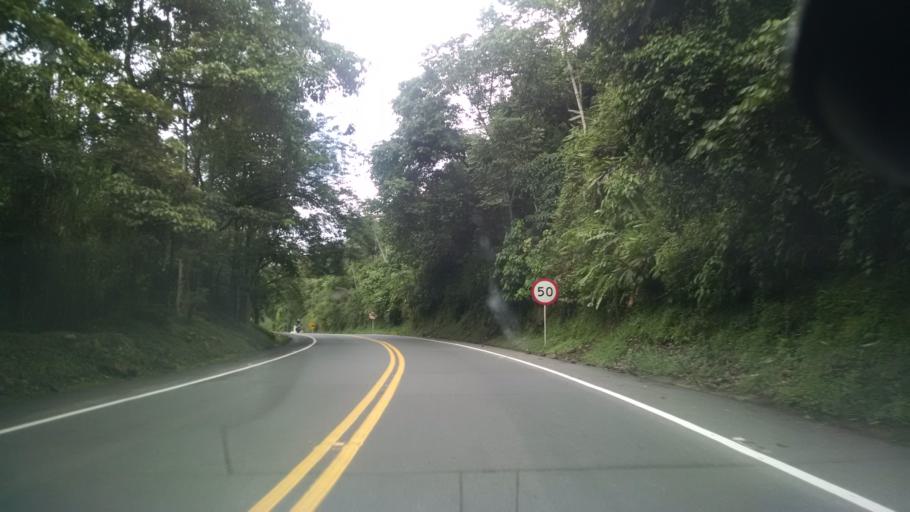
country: CO
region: Caldas
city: Palestina
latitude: 5.0470
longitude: -75.5968
